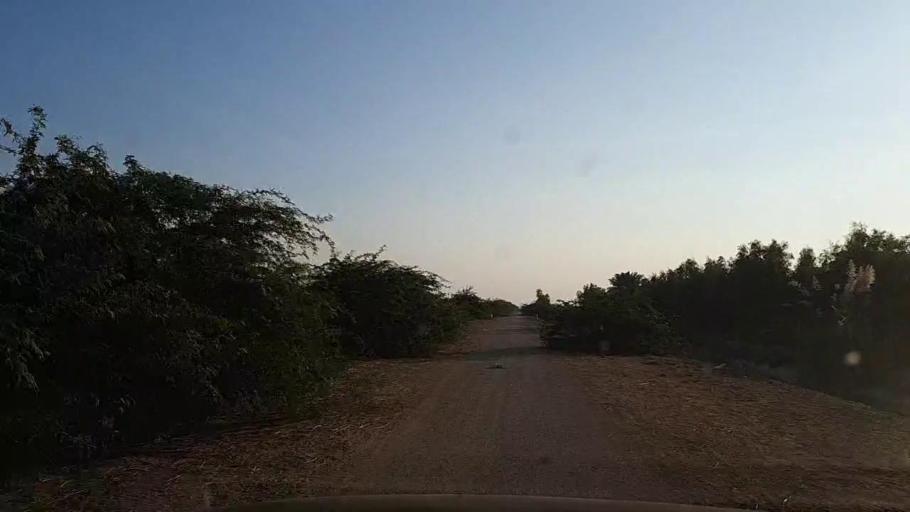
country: PK
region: Sindh
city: Thatta
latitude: 24.6176
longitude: 67.9120
